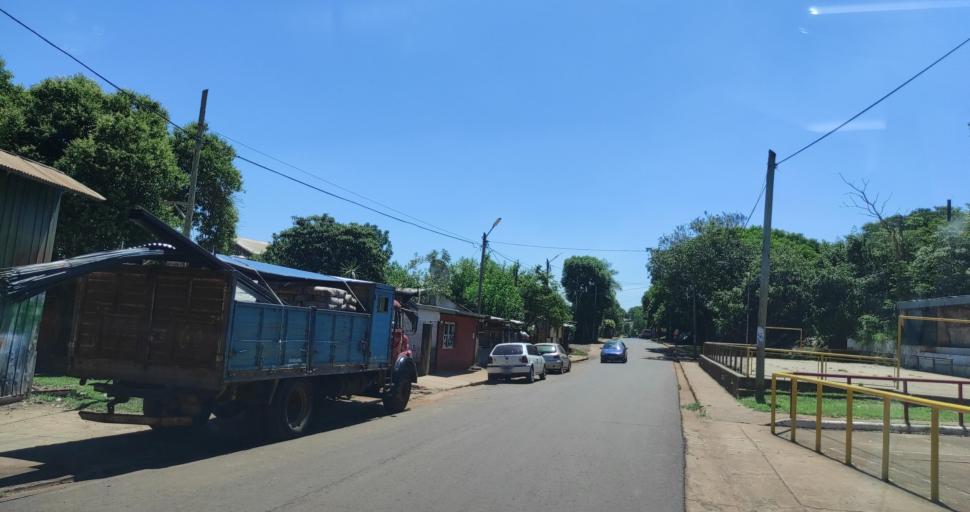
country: AR
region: Misiones
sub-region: Departamento de Capital
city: Posadas
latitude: -27.4173
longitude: -55.9056
